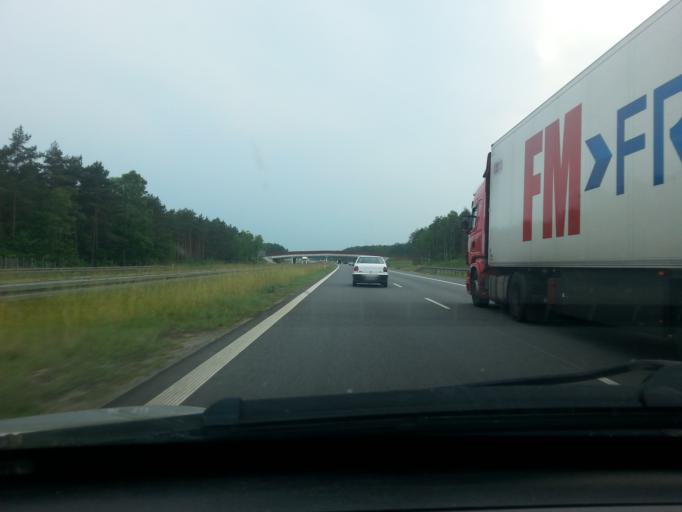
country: PL
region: Lodz Voivodeship
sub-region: Powiat skierniewicki
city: Bolimow
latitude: 52.0749
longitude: 20.2257
